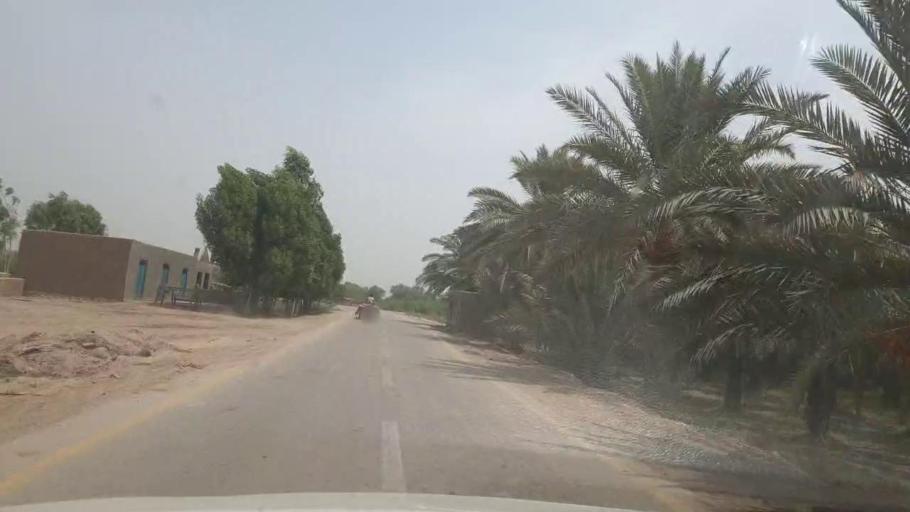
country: PK
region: Sindh
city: Kot Diji
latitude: 27.3910
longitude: 68.6602
